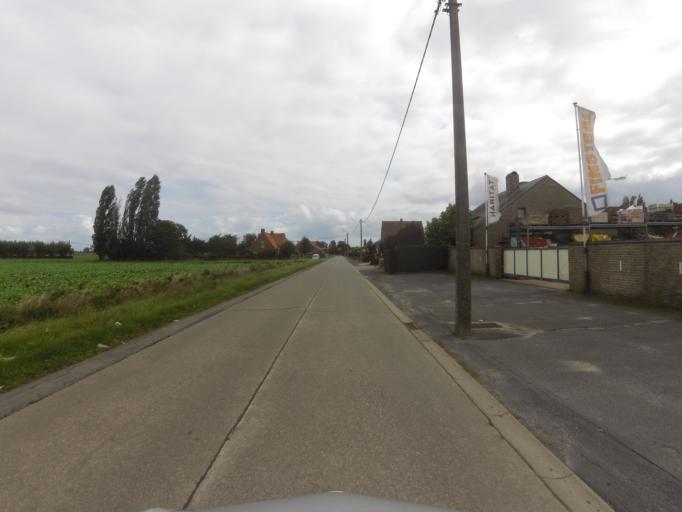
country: BE
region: Flanders
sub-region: Provincie West-Vlaanderen
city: Wingene
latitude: 51.0558
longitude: 3.2939
